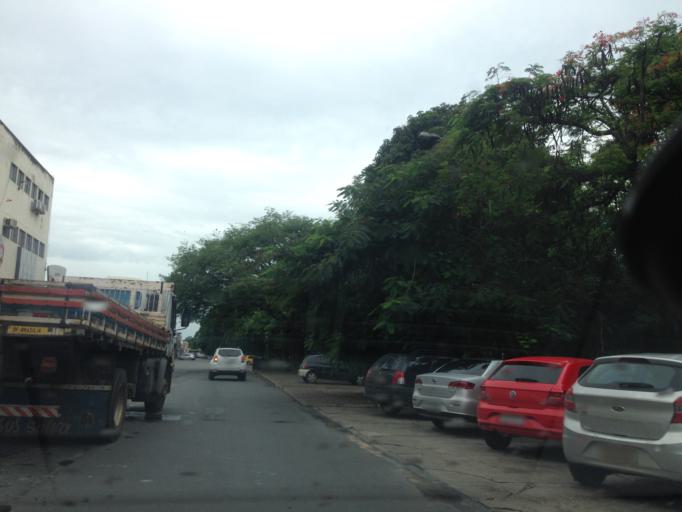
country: BR
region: Federal District
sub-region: Brasilia
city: Brasilia
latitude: -15.8092
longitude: -47.9011
